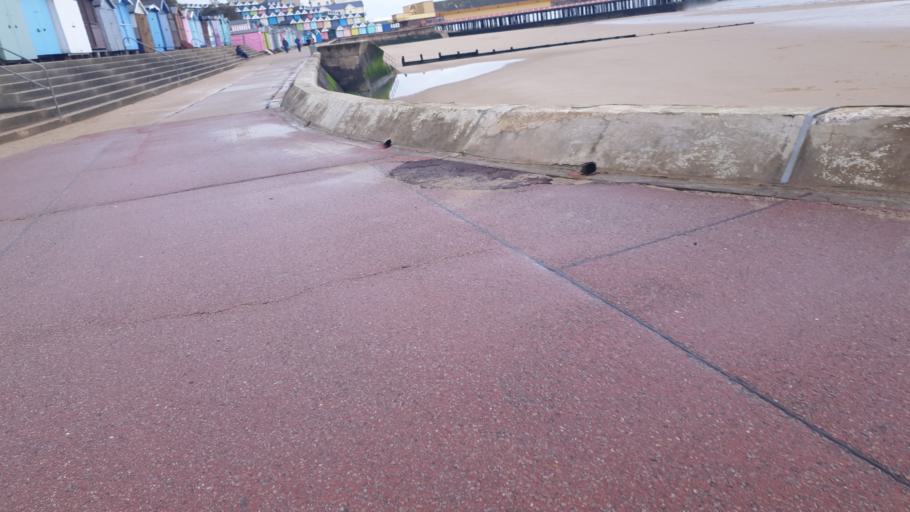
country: GB
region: England
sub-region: Essex
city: Walton-on-the-Naze
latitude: 51.8445
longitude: 1.2683
